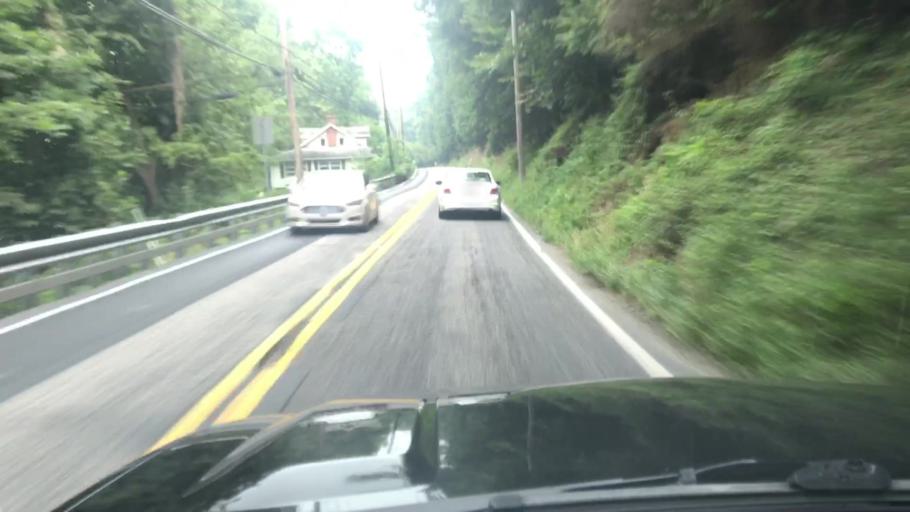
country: US
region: Pennsylvania
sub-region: Cumberland County
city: Shiremanstown
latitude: 40.2469
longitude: -76.9726
